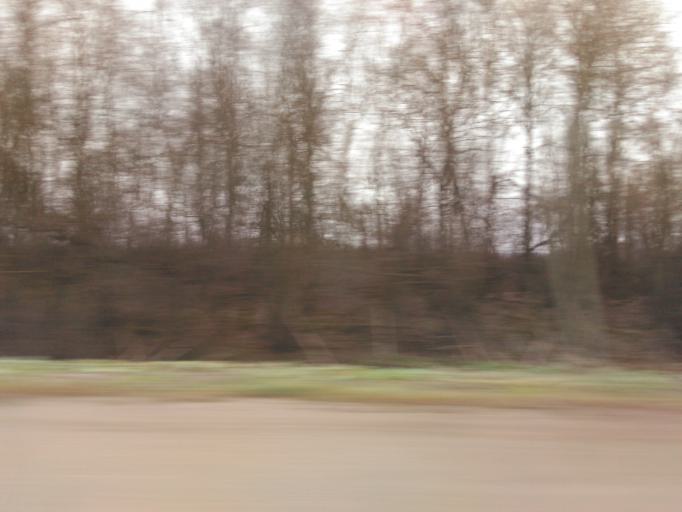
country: RU
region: Moskovskaya
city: Ashukino
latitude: 56.1367
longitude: 37.9842
